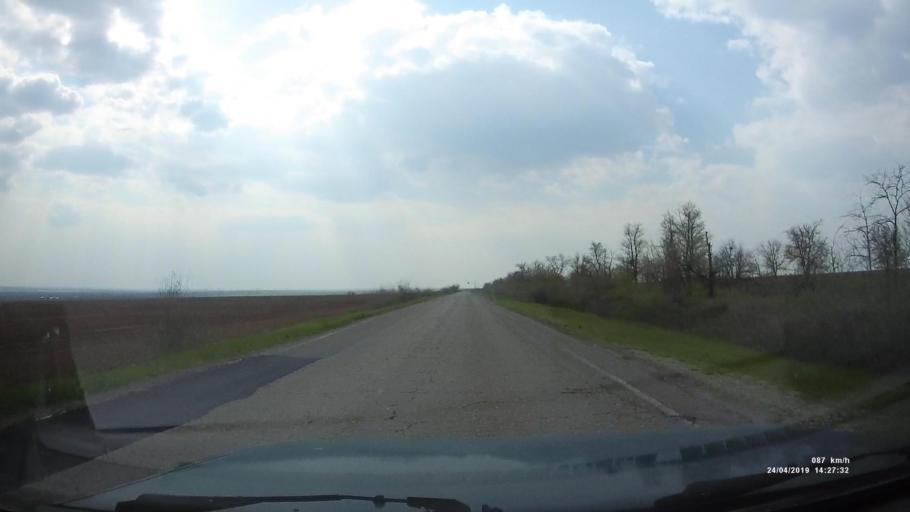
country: RU
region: Kalmykiya
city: Arshan'
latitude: 46.3339
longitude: 44.0413
